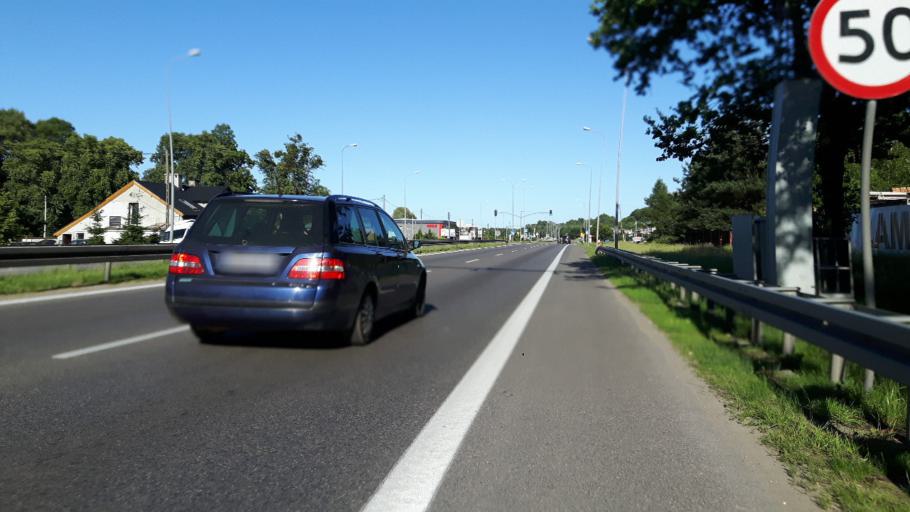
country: PL
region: Pomeranian Voivodeship
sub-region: Powiat wejherowski
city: Reda
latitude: 54.6048
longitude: 18.3158
